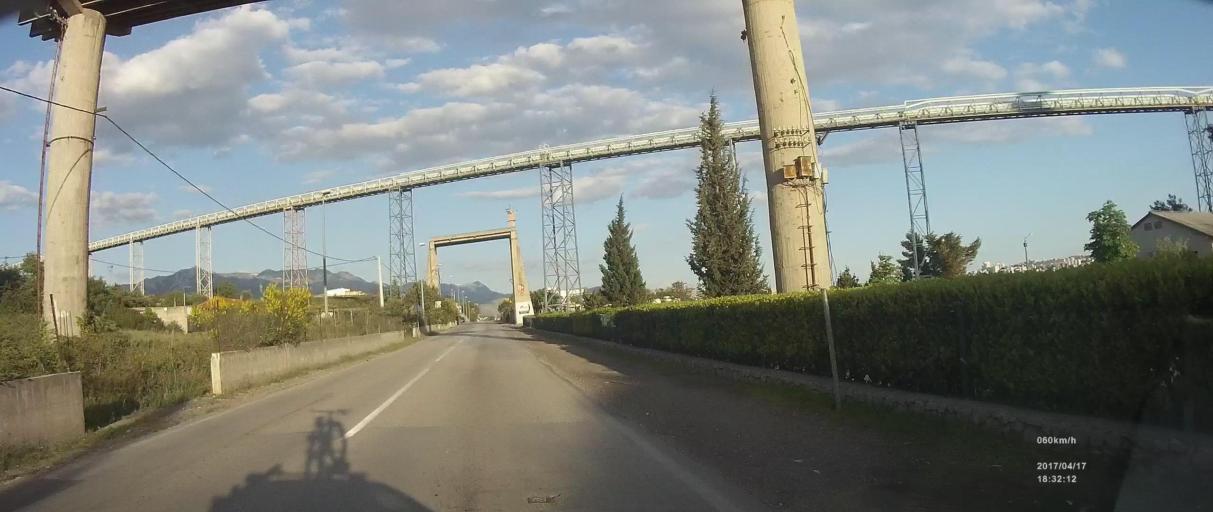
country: HR
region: Splitsko-Dalmatinska
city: Vranjic
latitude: 43.5431
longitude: 16.4428
